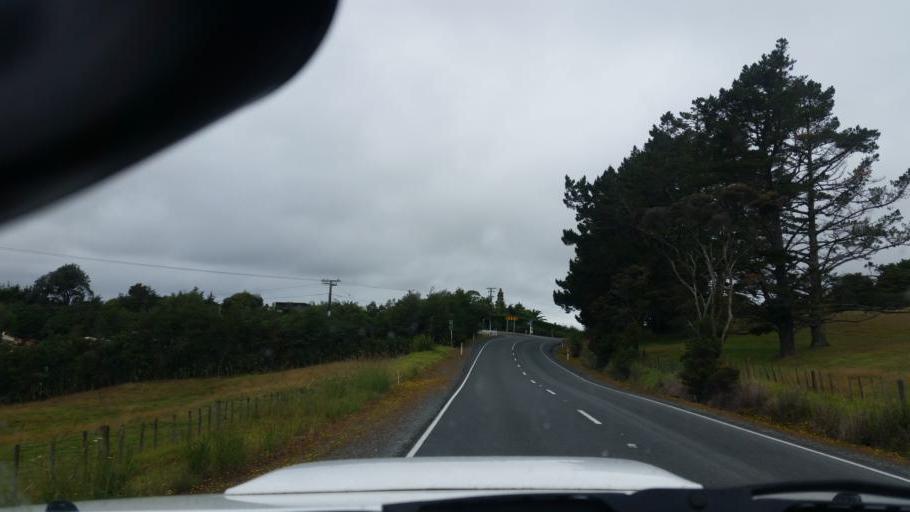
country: NZ
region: Auckland
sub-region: Auckland
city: Wellsford
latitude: -36.1330
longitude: 174.5384
